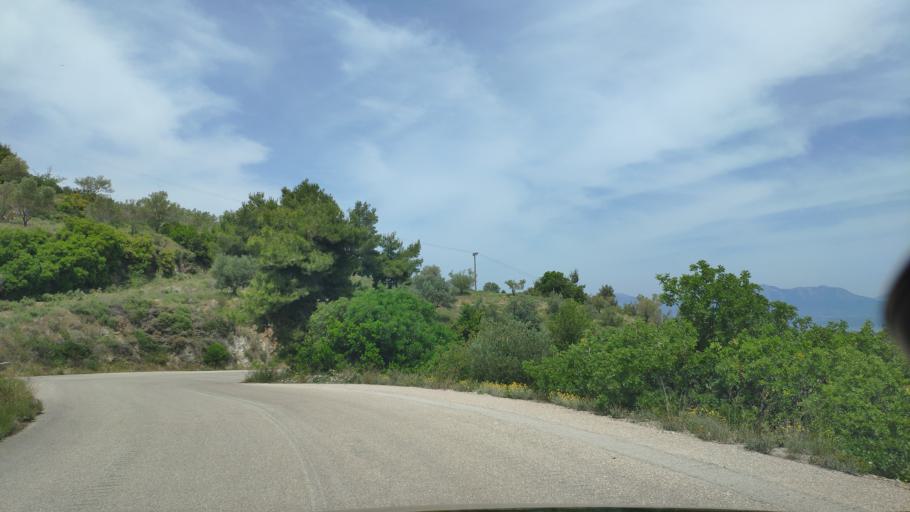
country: GR
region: Attica
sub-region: Nomarchia Anatolikis Attikis
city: Grammatiko
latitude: 38.2575
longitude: 23.9670
